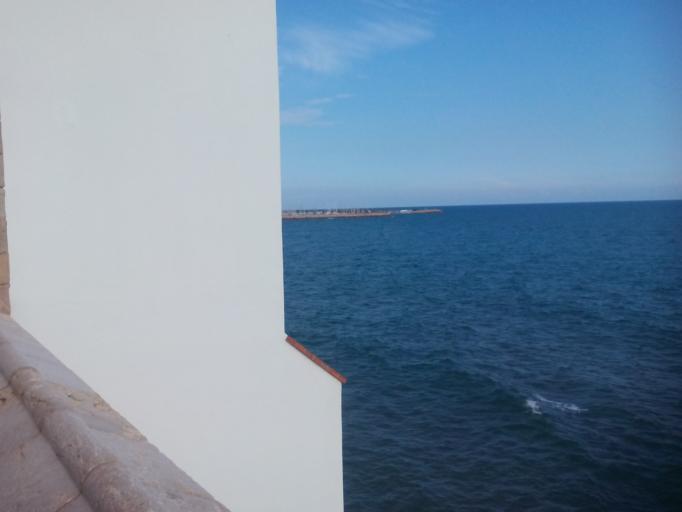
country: ES
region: Catalonia
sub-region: Provincia de Barcelona
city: Sitges
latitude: 41.2339
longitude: 1.8120
